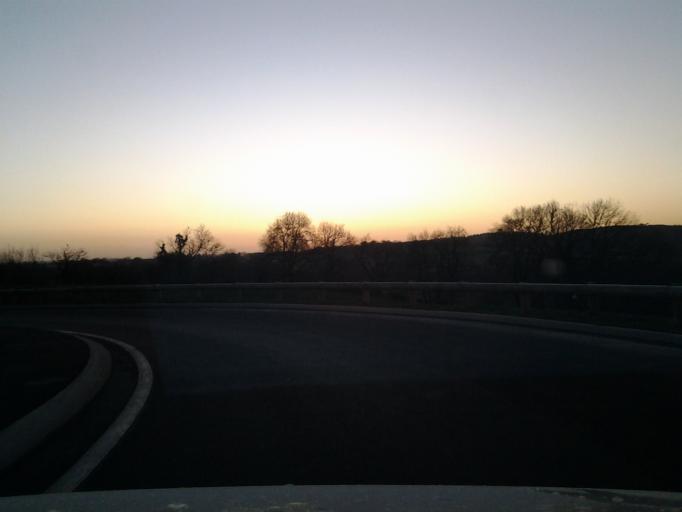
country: FR
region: Pays de la Loire
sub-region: Departement de la Vendee
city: Les Epesses
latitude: 46.8762
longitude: -0.9267
